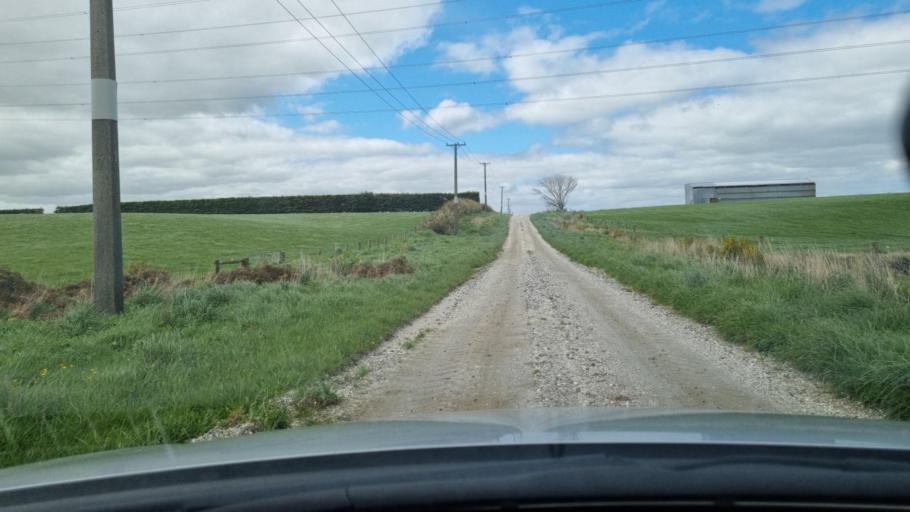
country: NZ
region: Southland
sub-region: Invercargill City
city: Invercargill
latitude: -46.4429
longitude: 168.4515
